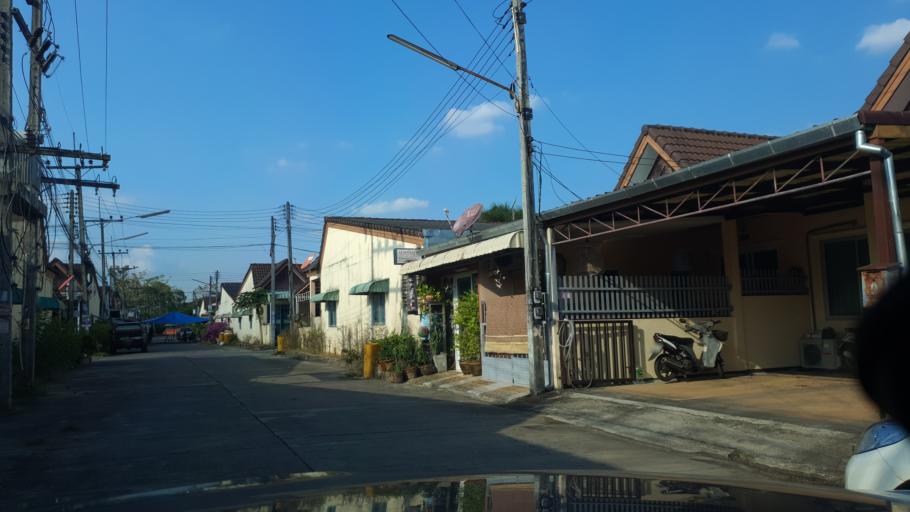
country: TH
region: Krabi
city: Nuea Khlong
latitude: 8.0819
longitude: 98.9891
